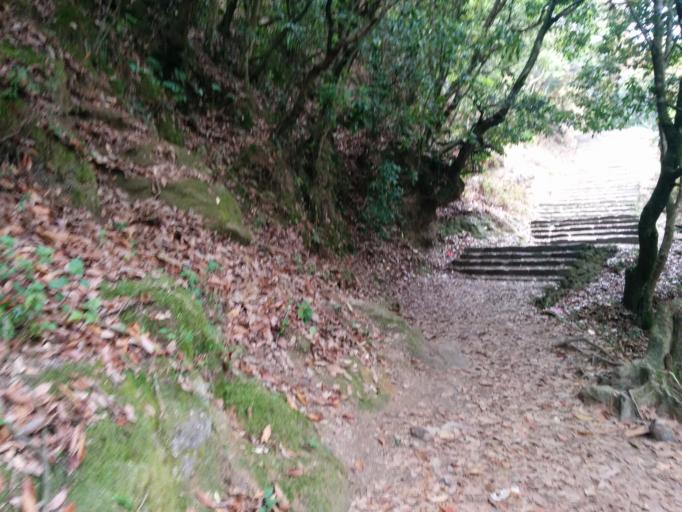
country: NP
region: Central Region
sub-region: Bagmati Zone
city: Bhaktapur
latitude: 27.7700
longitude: 85.4252
